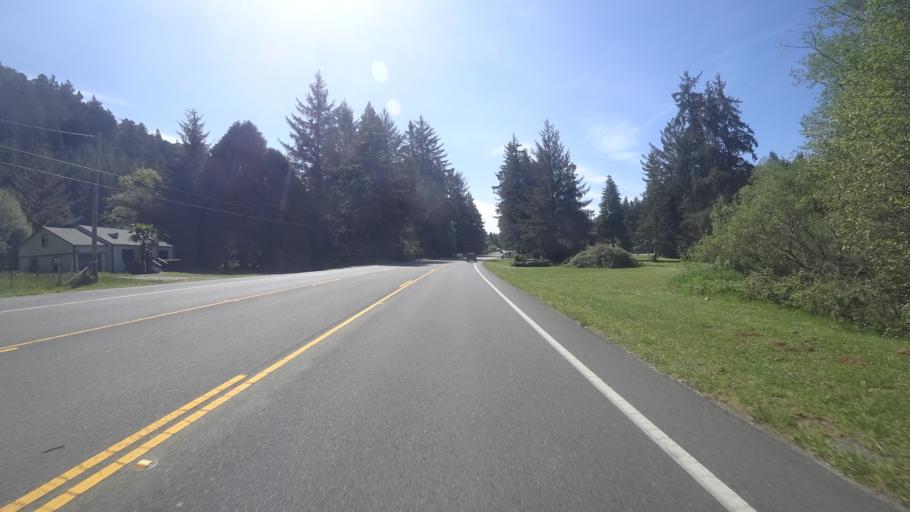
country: US
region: California
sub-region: Del Norte County
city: Bertsch-Oceanview
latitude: 41.5775
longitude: -124.0744
